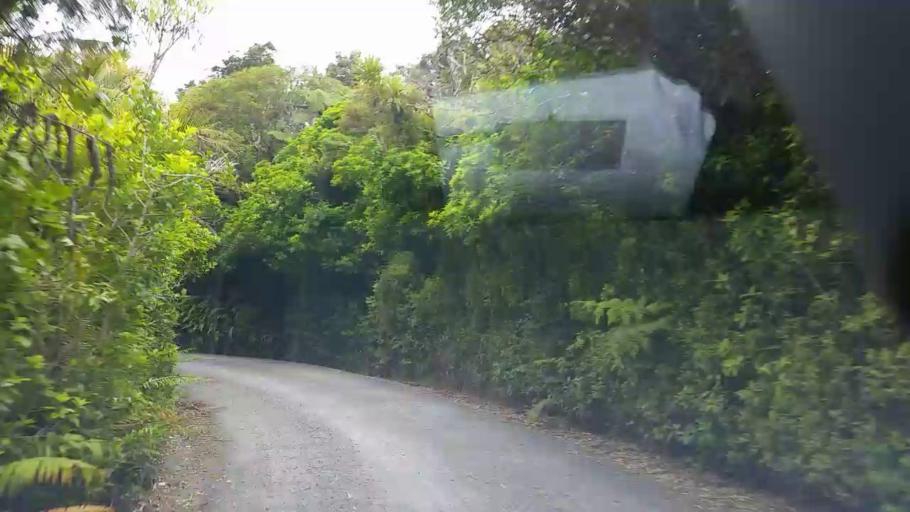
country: NZ
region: Auckland
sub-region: Auckland
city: Muriwai Beach
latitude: -36.9257
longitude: 174.4981
